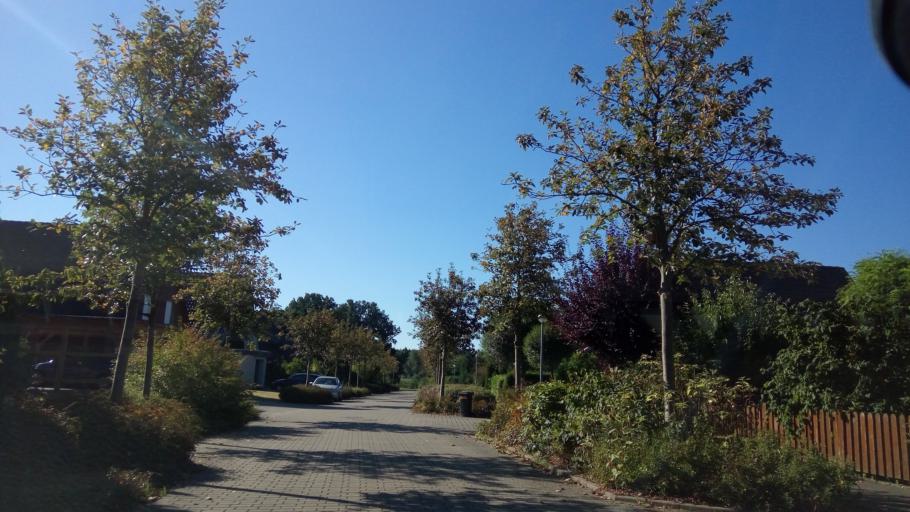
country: DE
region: Lower Saxony
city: Emmendorf
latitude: 52.9975
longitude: 10.5222
